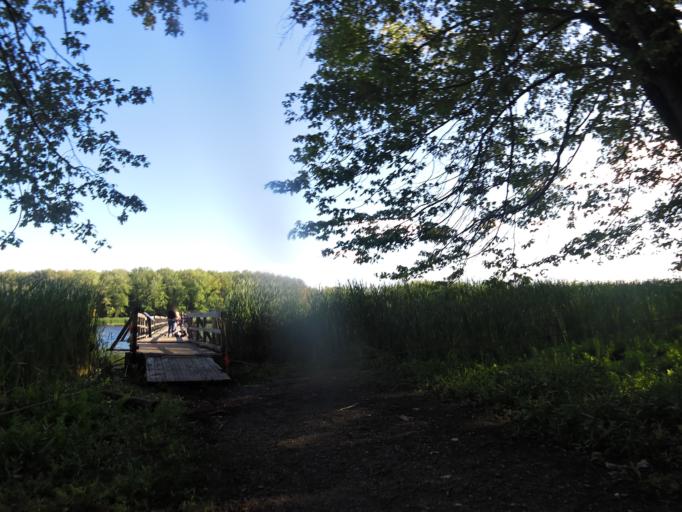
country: CA
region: Quebec
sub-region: Outaouais
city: Gatineau
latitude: 45.4840
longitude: -75.5915
